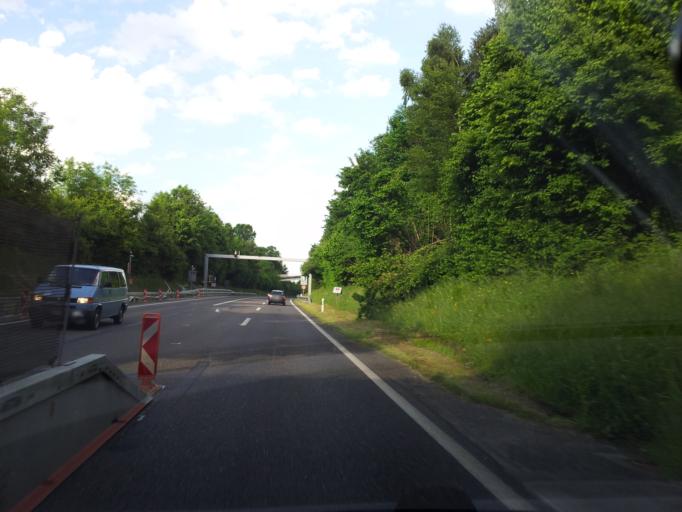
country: CH
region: Bern
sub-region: Interlaken-Oberhasli District
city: Bonigen
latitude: 46.6827
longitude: 7.8912
